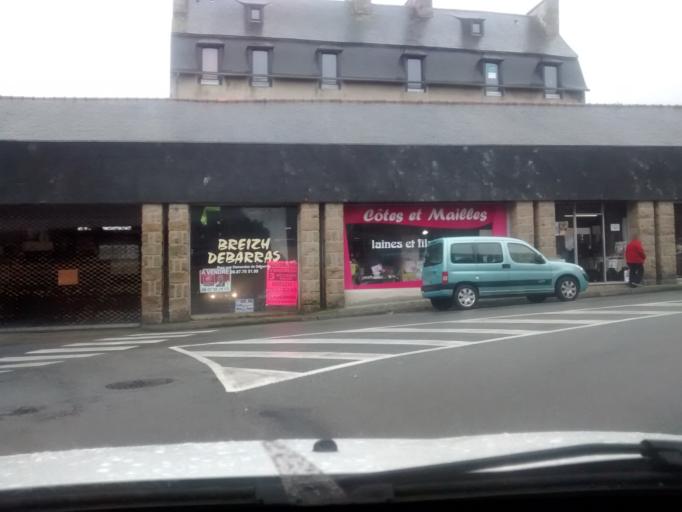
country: FR
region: Brittany
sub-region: Departement des Cotes-d'Armor
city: Treguier
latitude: 48.7858
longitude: -3.2309
